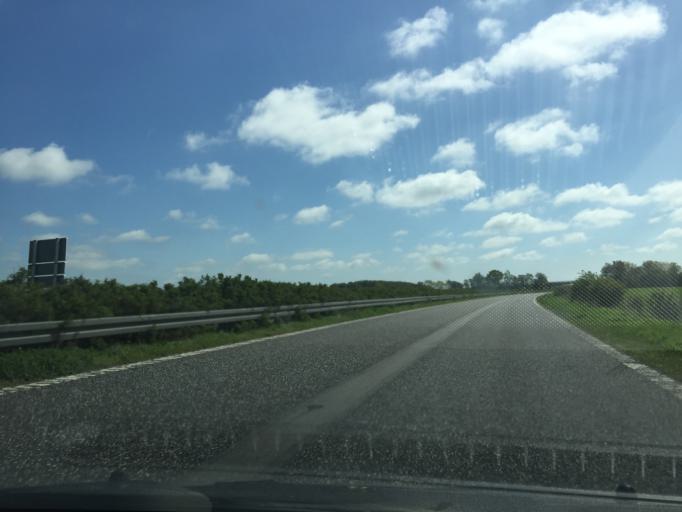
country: DK
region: Zealand
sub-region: Lolland Kommune
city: Maribo
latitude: 54.7557
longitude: 11.4616
